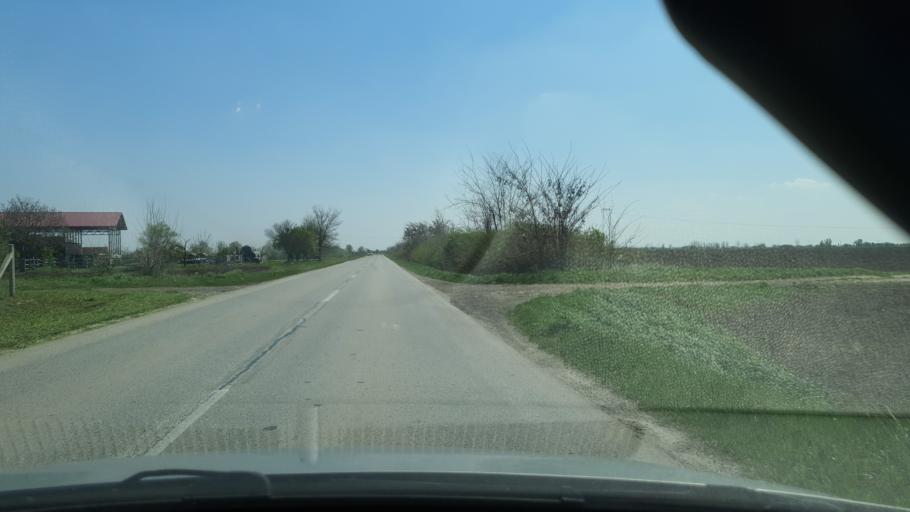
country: RS
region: Autonomna Pokrajina Vojvodina
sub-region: Zapadnobacki Okrug
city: Odzaci
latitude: 45.4928
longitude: 19.2782
